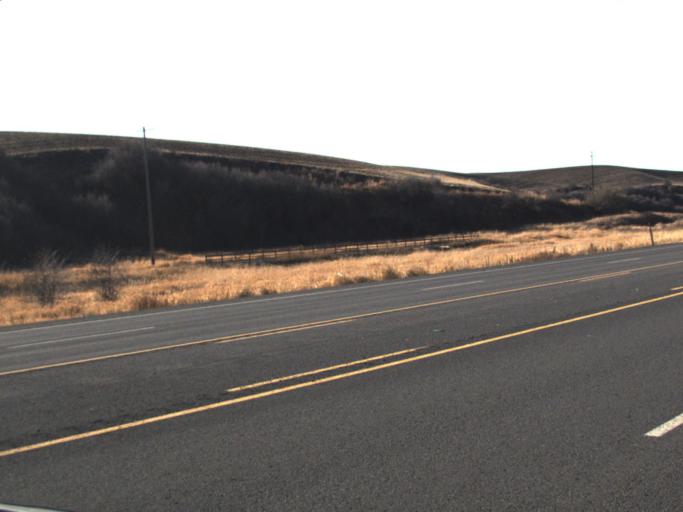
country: US
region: Washington
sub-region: Whitman County
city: Pullman
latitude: 46.7296
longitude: -117.0969
